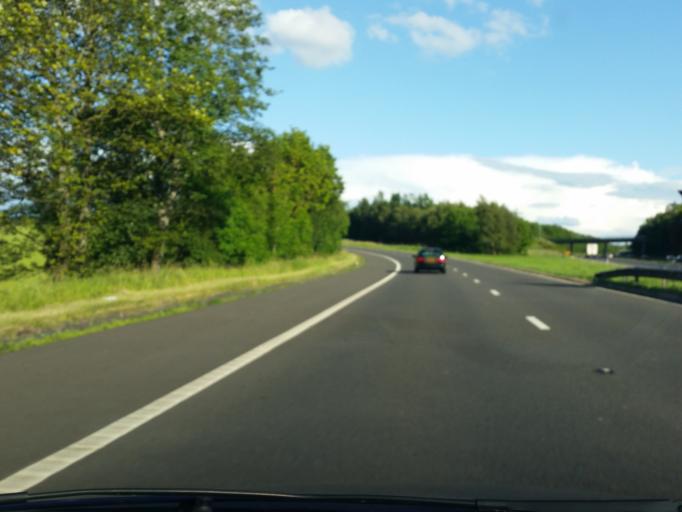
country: GB
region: Scotland
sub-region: South Lanarkshire
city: Larkhall
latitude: 55.7563
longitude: -3.9725
